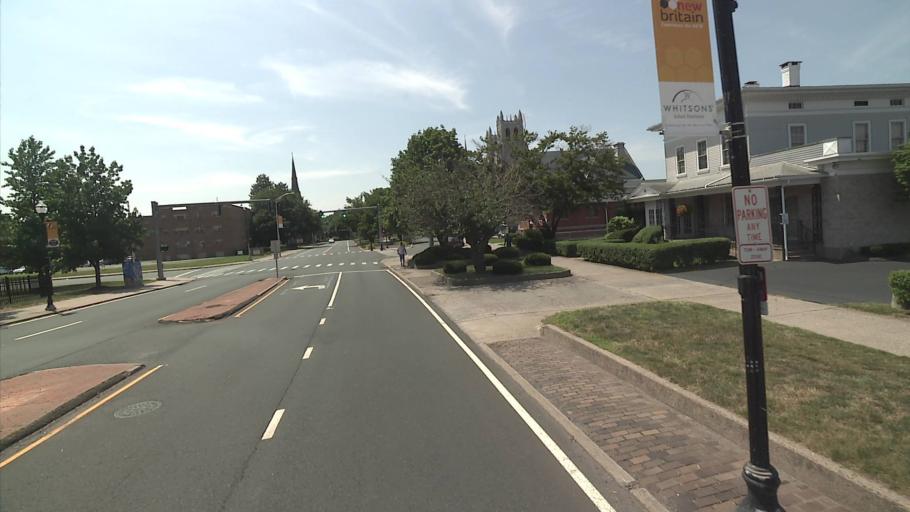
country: US
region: Connecticut
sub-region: Hartford County
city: New Britain
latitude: 41.6635
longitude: -72.7800
